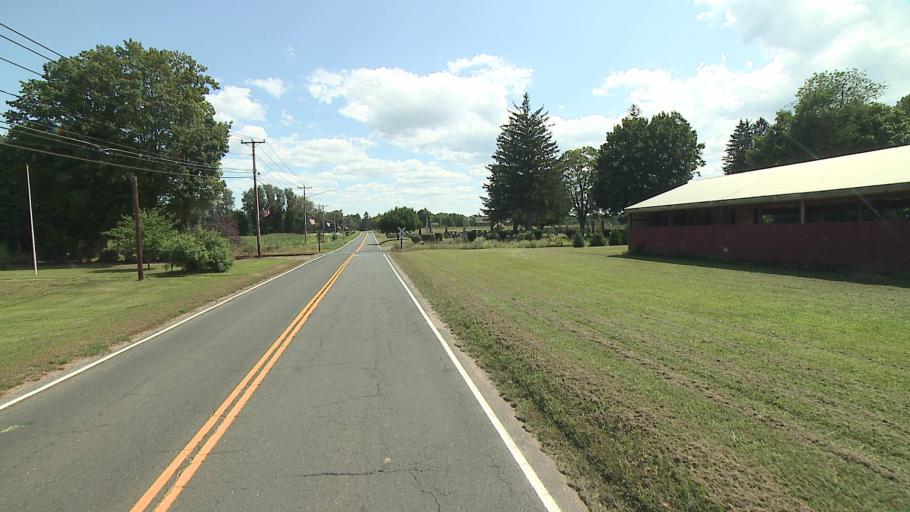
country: US
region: Connecticut
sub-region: Hartford County
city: Broad Brook
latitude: 41.9375
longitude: -72.5259
